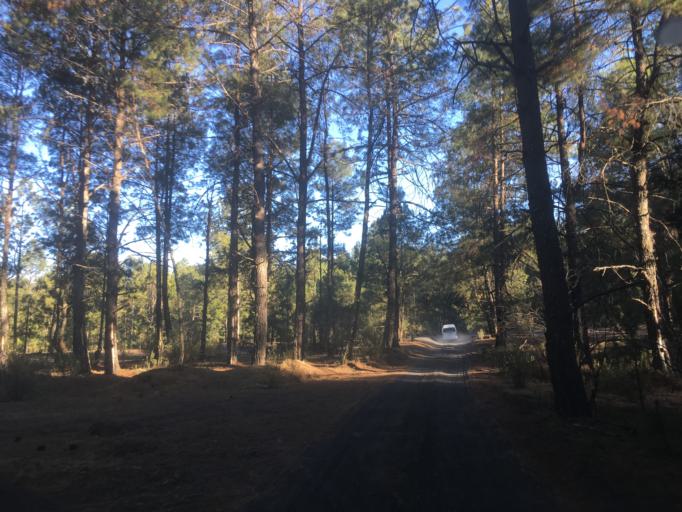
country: MX
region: Michoacan
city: Angahuan
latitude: 19.4650
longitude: -102.2399
